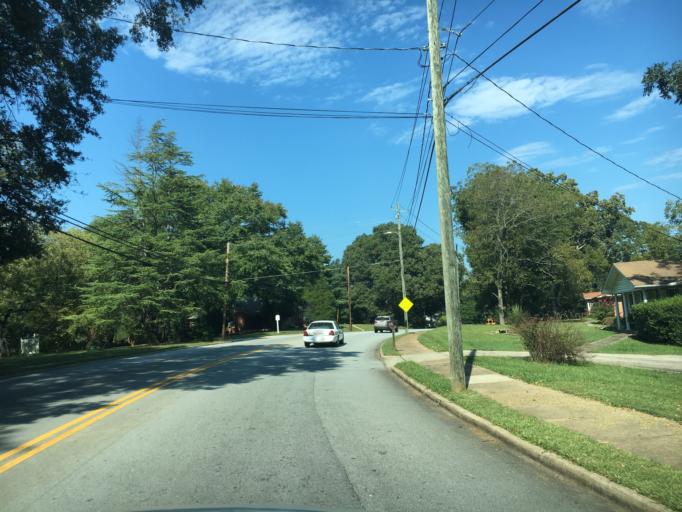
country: US
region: Georgia
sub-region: Franklin County
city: Lavonia
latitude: 34.4429
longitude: -83.1076
